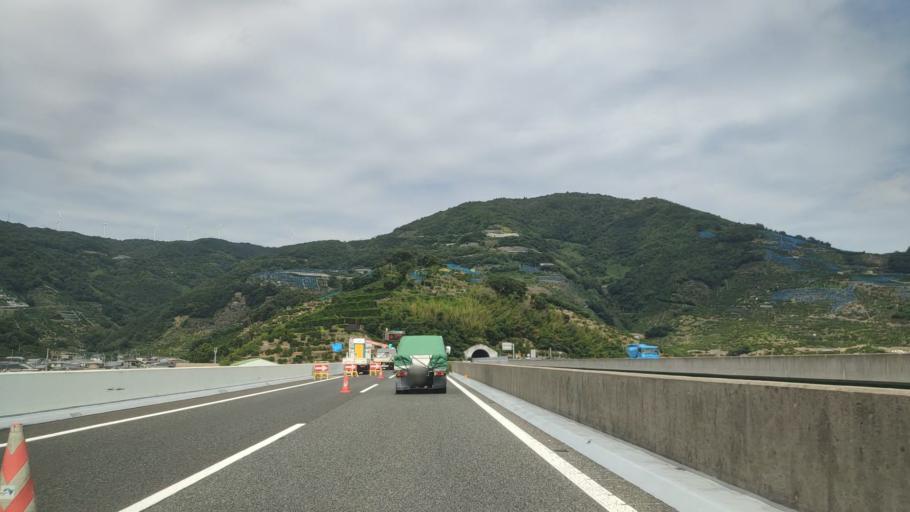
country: JP
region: Wakayama
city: Kainan
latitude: 34.0741
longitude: 135.2007
